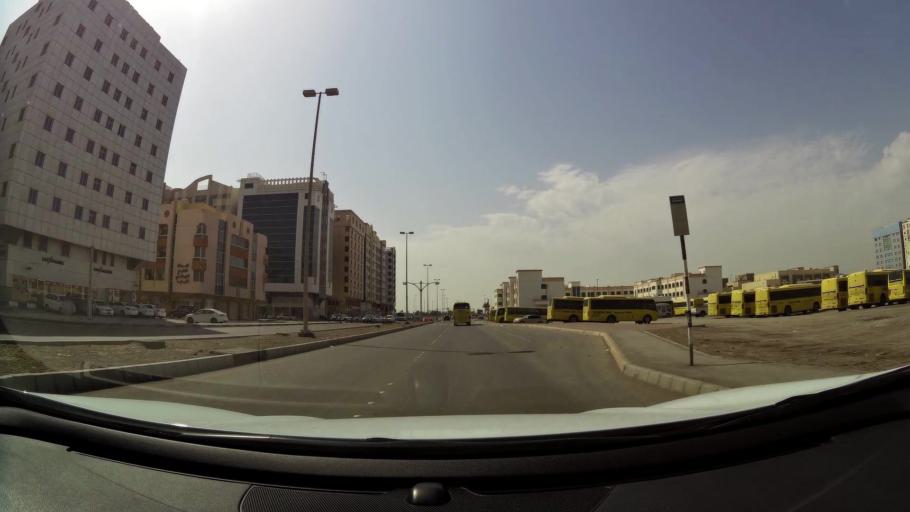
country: AE
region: Abu Dhabi
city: Abu Dhabi
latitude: 24.3380
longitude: 54.5326
